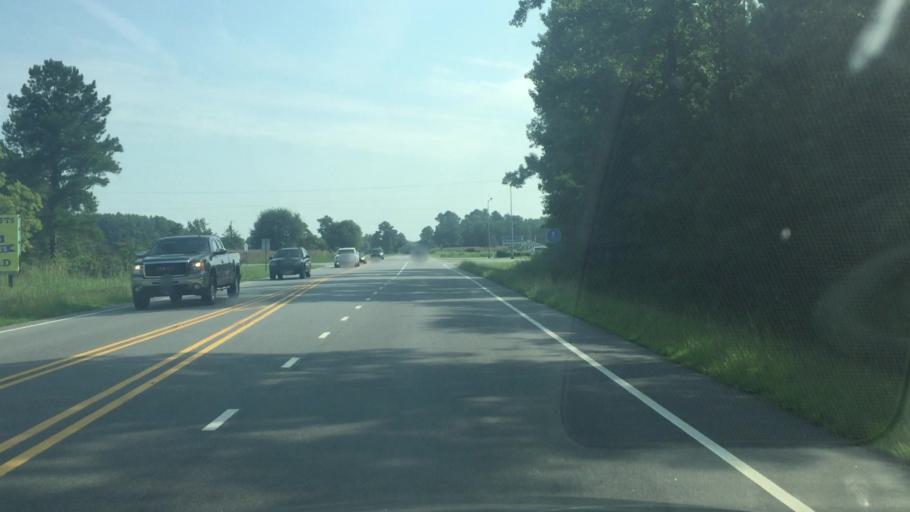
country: US
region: North Carolina
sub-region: Columbus County
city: Tabor City
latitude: 34.2012
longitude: -78.8322
